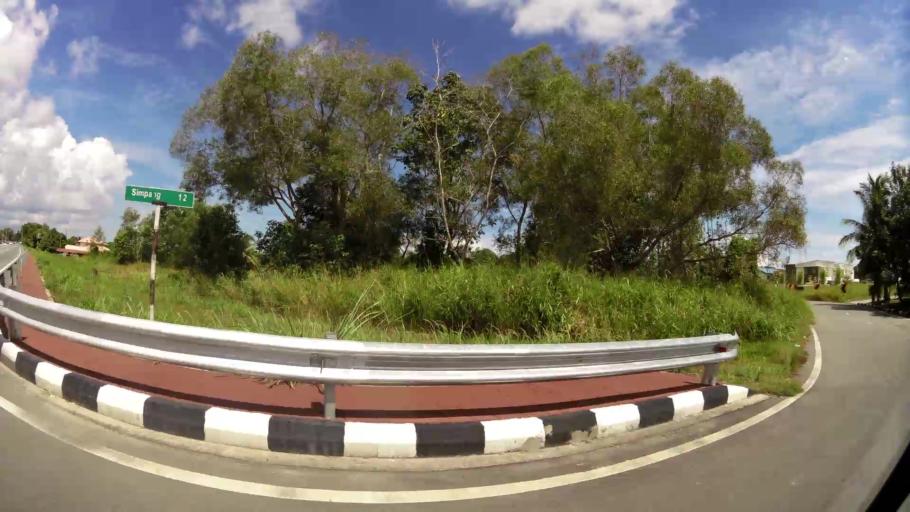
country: BN
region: Brunei and Muara
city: Bandar Seri Begawan
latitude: 4.9406
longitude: 114.9053
